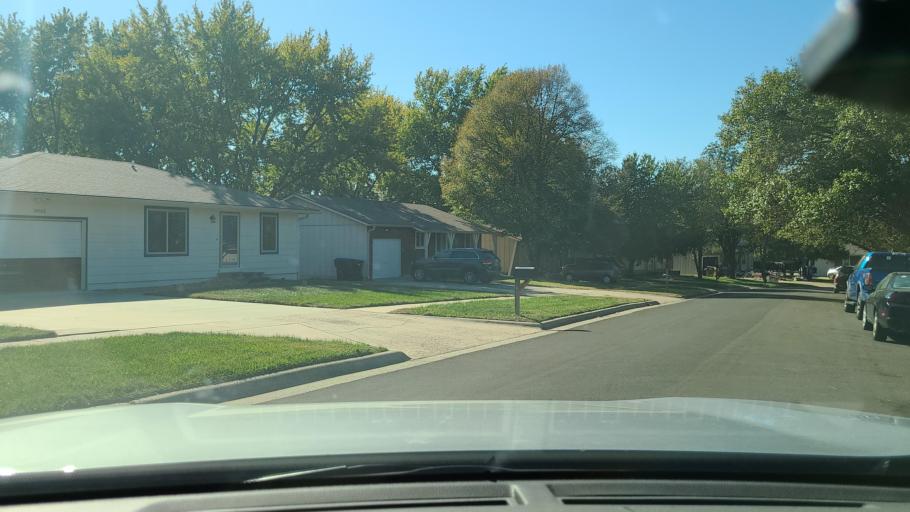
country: US
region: Kansas
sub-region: Shawnee County
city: Topeka
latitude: 38.9966
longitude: -95.7213
